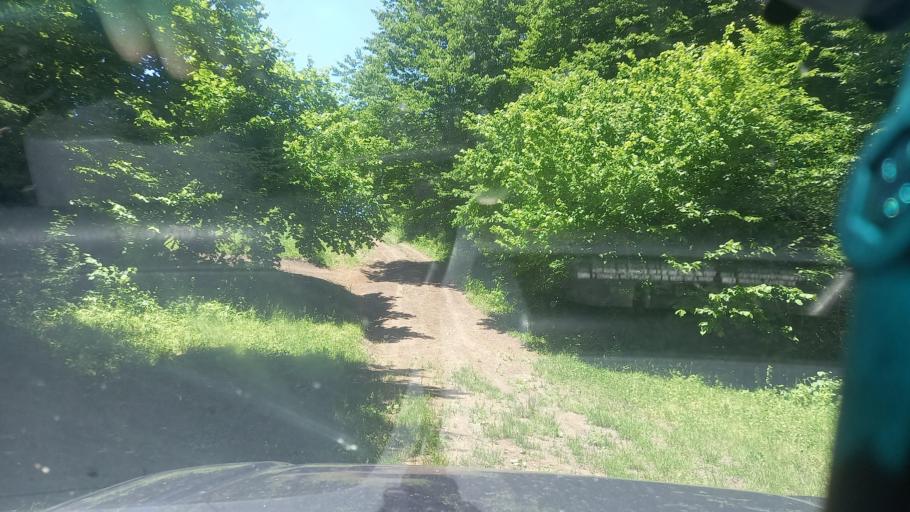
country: RU
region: Karachayevo-Cherkesiya
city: Pregradnaya
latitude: 44.1043
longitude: 41.1383
